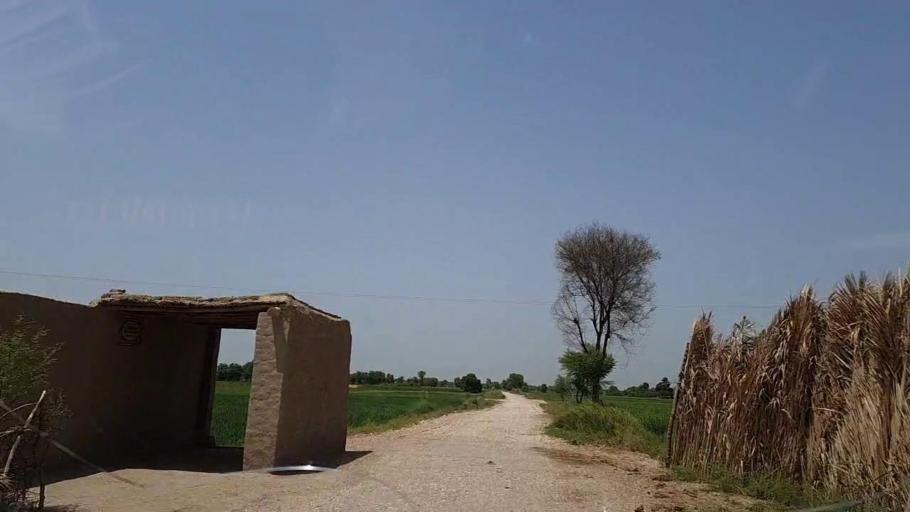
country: PK
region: Sindh
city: Tharu Shah
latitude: 26.9492
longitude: 68.0437
